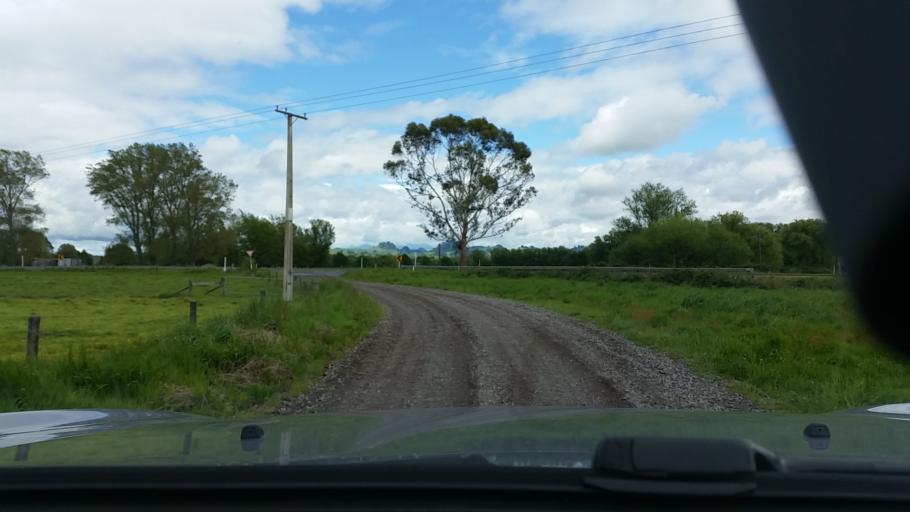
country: NZ
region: Bay of Plenty
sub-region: Rotorua District
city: Rotorua
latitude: -38.4169
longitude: 176.3485
